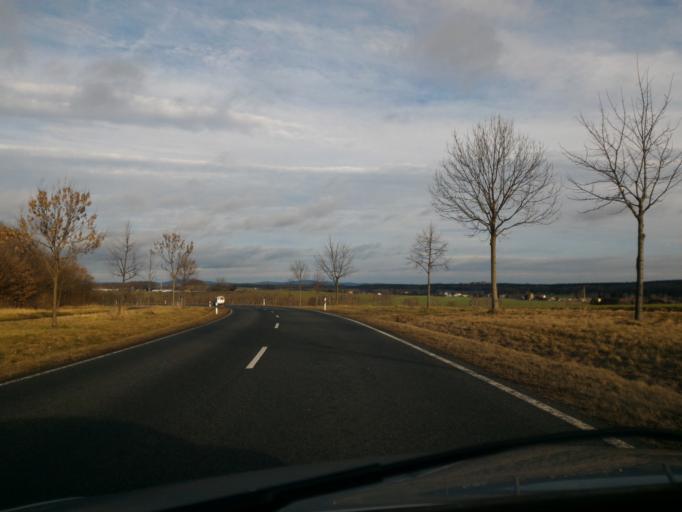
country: DE
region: Saxony
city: Neugersdorf
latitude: 50.9877
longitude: 14.6247
